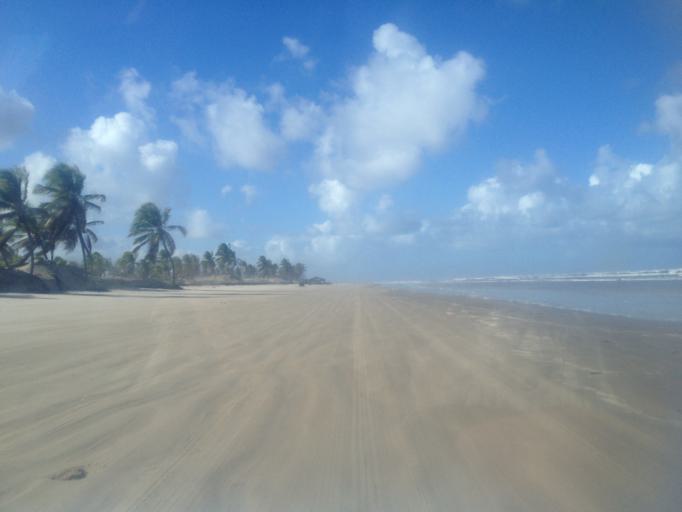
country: BR
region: Sergipe
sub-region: Indiaroba
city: Indiaroba
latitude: -11.4701
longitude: -37.3569
